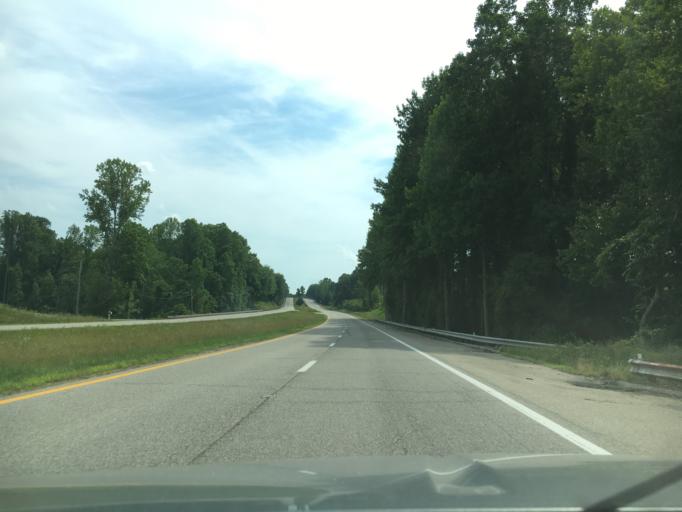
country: US
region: Virginia
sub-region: Lunenburg County
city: Victoria
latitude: 37.1134
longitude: -78.3485
